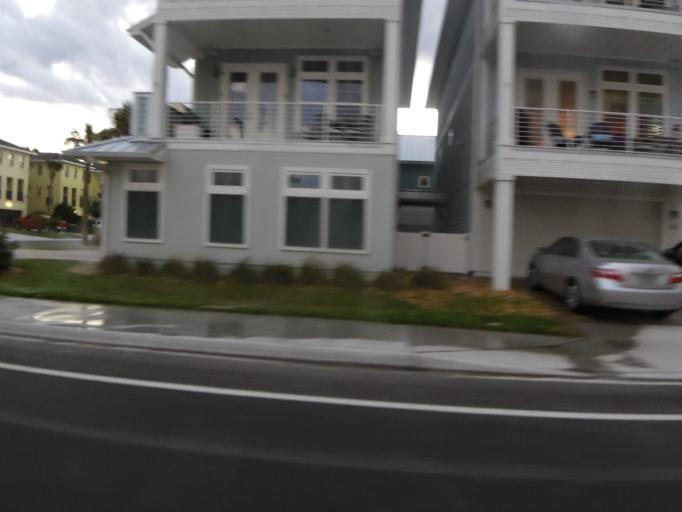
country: US
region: Florida
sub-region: Duval County
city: Jacksonville Beach
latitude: 30.2858
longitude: -81.3890
